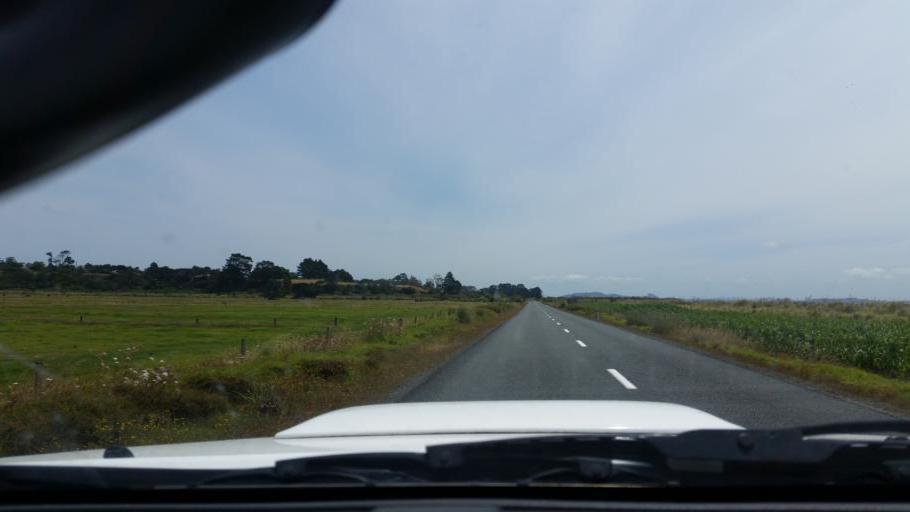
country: NZ
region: Northland
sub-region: Kaipara District
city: Dargaville
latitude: -36.1807
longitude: 174.0306
